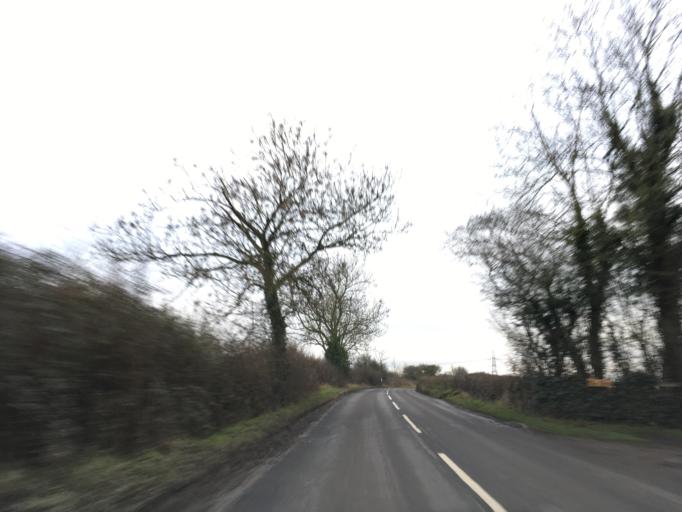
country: GB
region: England
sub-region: South Gloucestershire
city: Alveston
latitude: 51.5631
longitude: -2.5096
